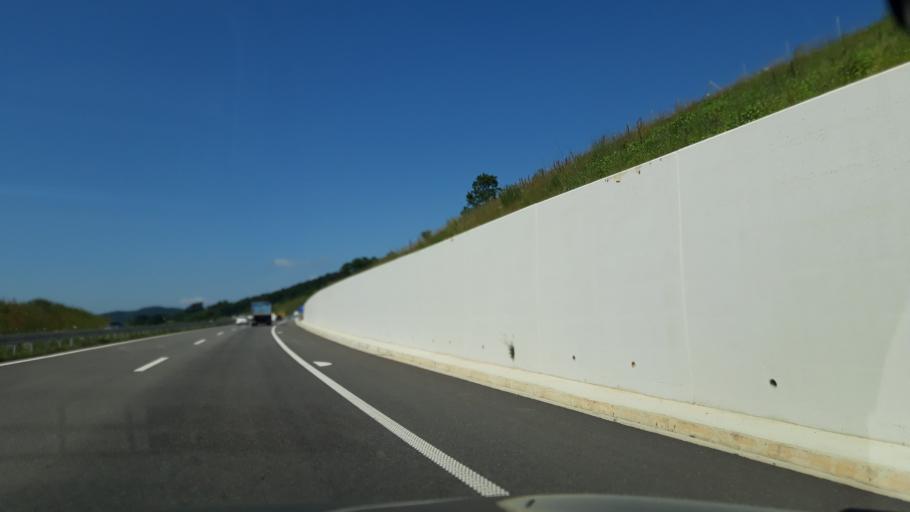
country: RS
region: Central Serbia
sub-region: Pcinjski Okrug
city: Vladicin Han
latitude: 42.6903
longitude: 22.0738
